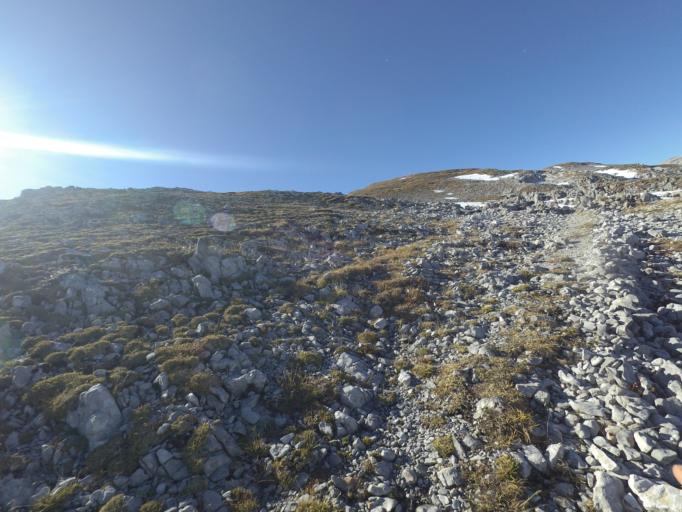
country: AT
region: Salzburg
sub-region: Politischer Bezirk Sankt Johann im Pongau
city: Werfenweng
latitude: 47.5015
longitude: 13.2324
